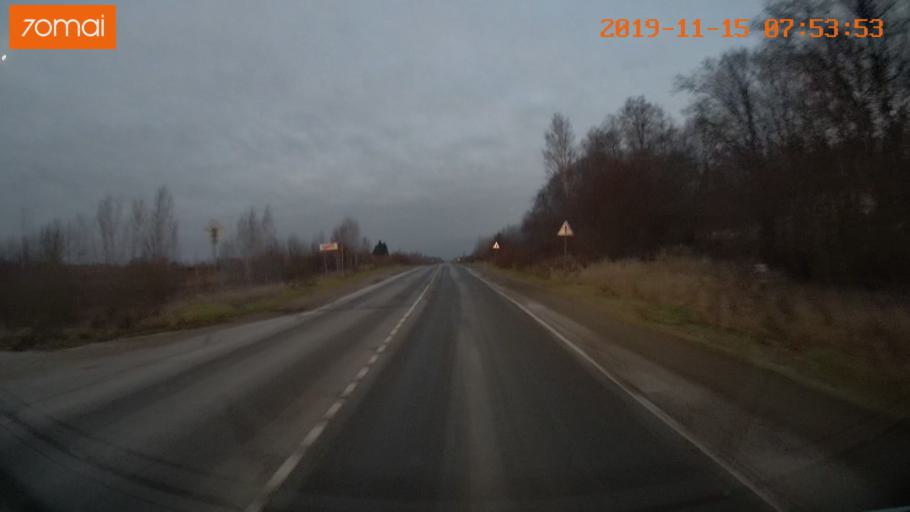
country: RU
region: Vologda
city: Cherepovets
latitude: 58.8935
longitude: 38.1819
